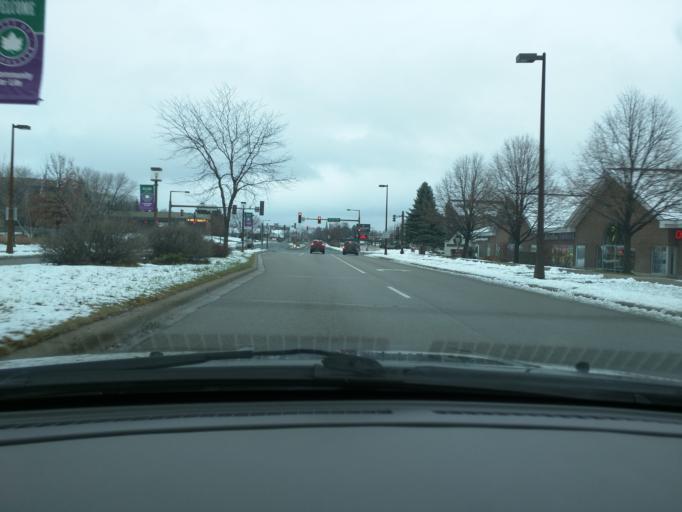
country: US
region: Minnesota
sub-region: Carver County
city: Chanhassen
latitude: 44.8622
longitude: -93.5391
